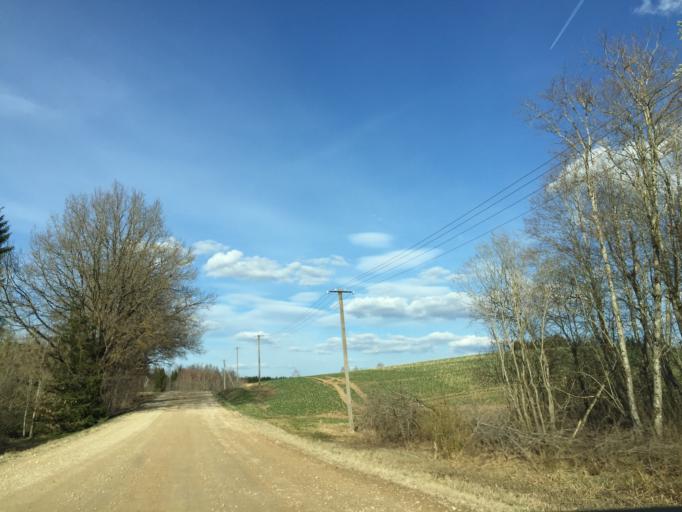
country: EE
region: Tartu
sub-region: Noo vald
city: Noo
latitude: 58.1146
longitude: 26.5559
